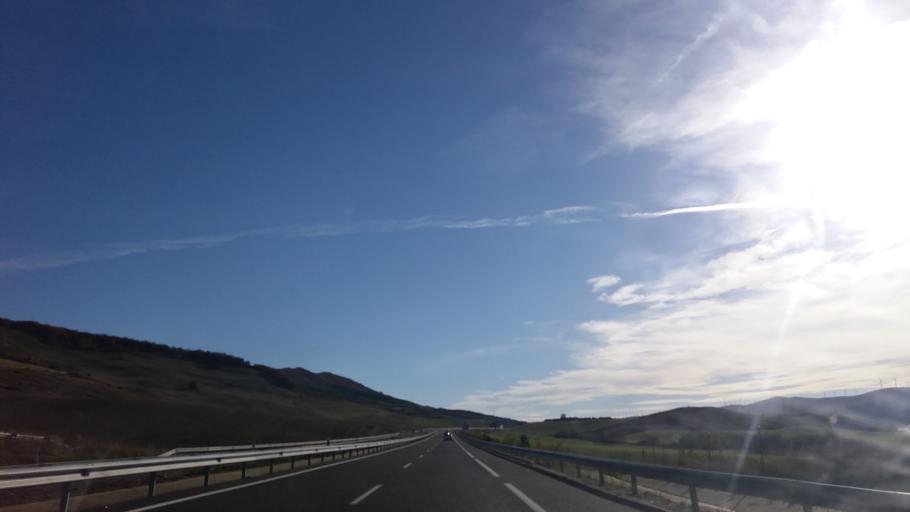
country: ES
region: Navarre
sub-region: Provincia de Navarra
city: Monreal
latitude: 42.7089
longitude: -1.5023
